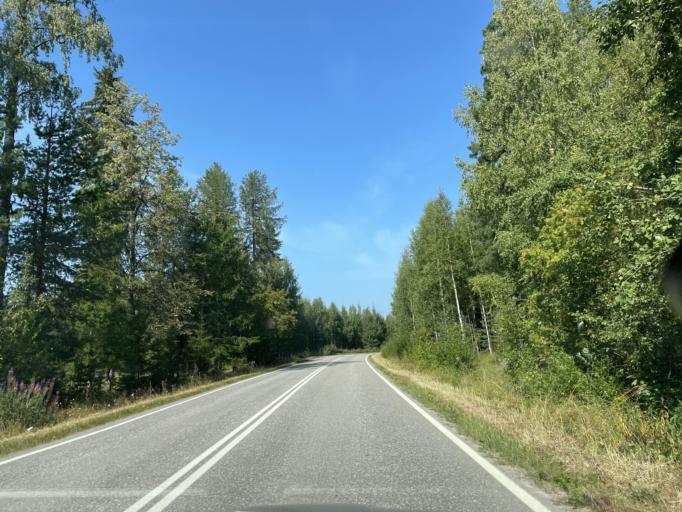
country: FI
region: Central Finland
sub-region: Saarijaervi-Viitasaari
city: Pihtipudas
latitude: 63.3707
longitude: 25.6174
